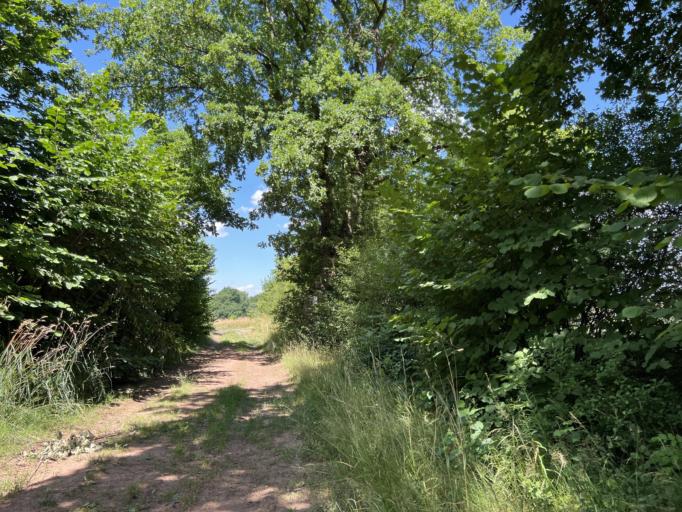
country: DE
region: Hesse
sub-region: Regierungsbezirk Darmstadt
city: Steinau an der Strasse
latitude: 50.2995
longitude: 9.4772
